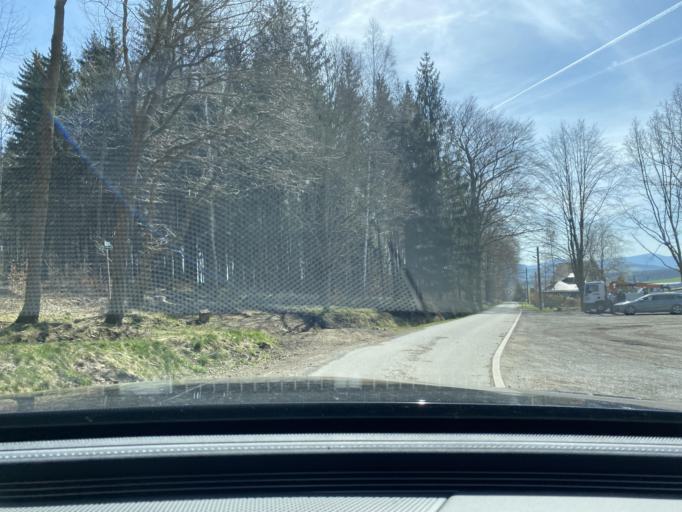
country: DE
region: Saxony
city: Eibau
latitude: 51.0053
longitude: 14.6493
